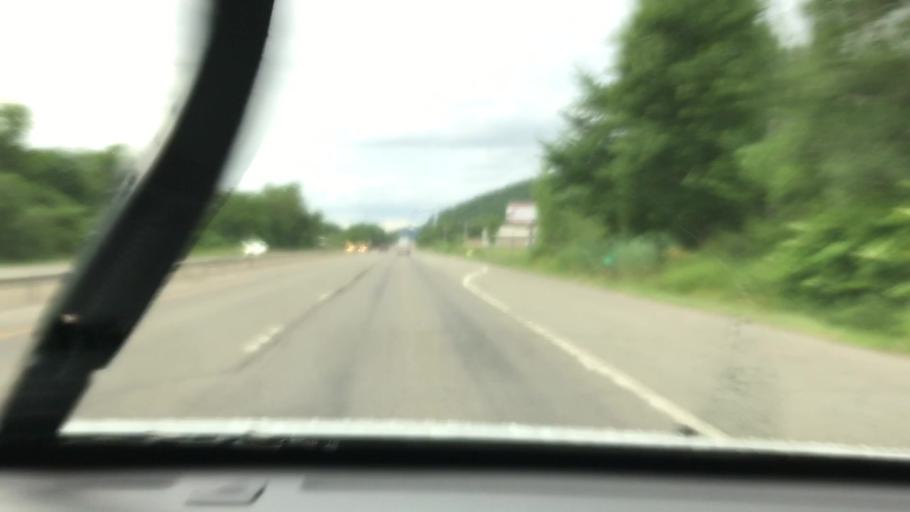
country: US
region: Pennsylvania
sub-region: McKean County
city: Foster Brook
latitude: 42.0418
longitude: -78.6334
